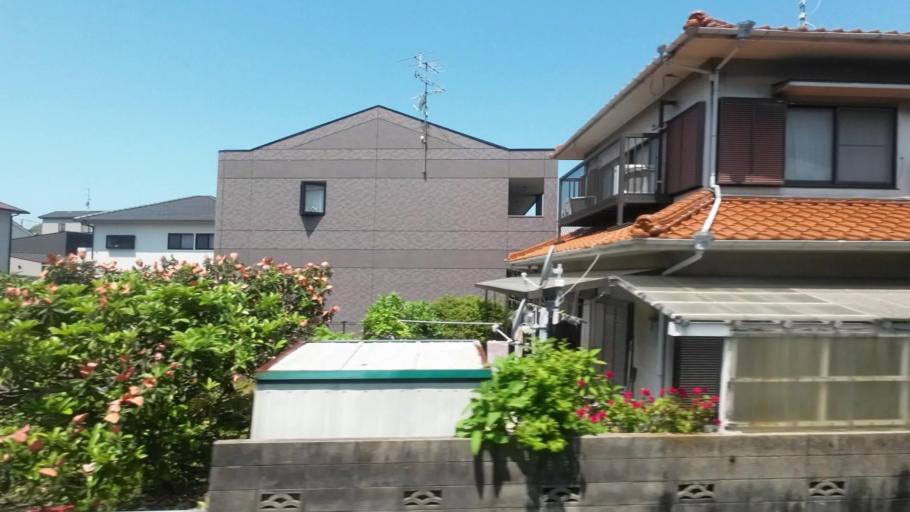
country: JP
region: Ehime
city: Hojo
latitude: 33.9771
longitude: 132.7774
